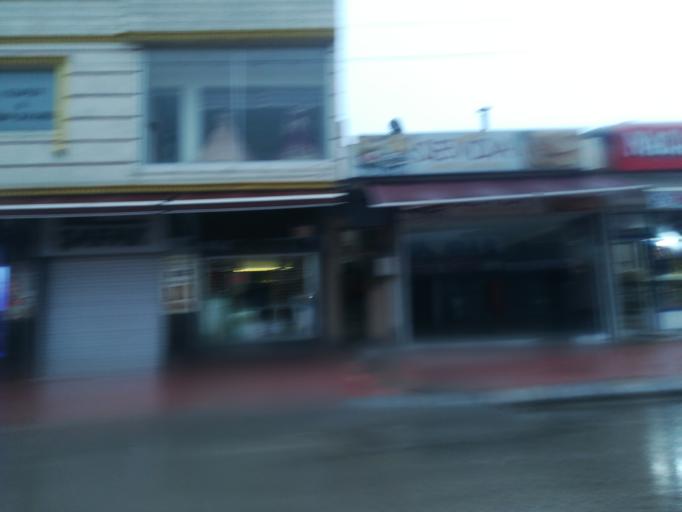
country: TR
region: Adana
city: Seyhan
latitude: 37.0188
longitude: 35.2976
